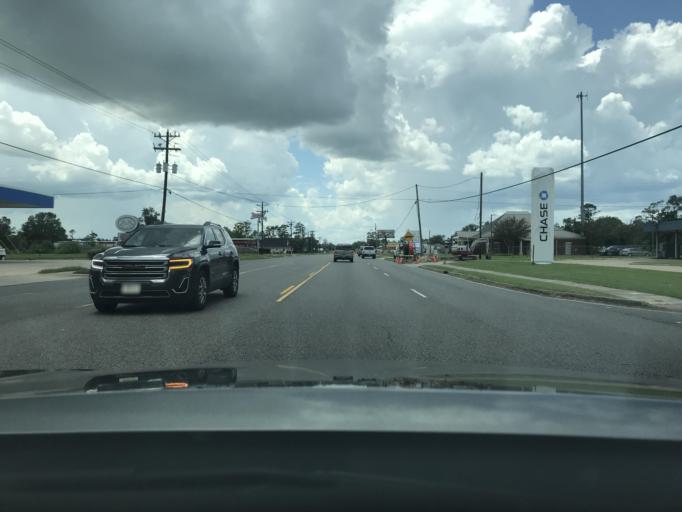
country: US
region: Louisiana
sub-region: Calcasieu Parish
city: Moss Bluff
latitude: 30.3007
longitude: -93.2057
